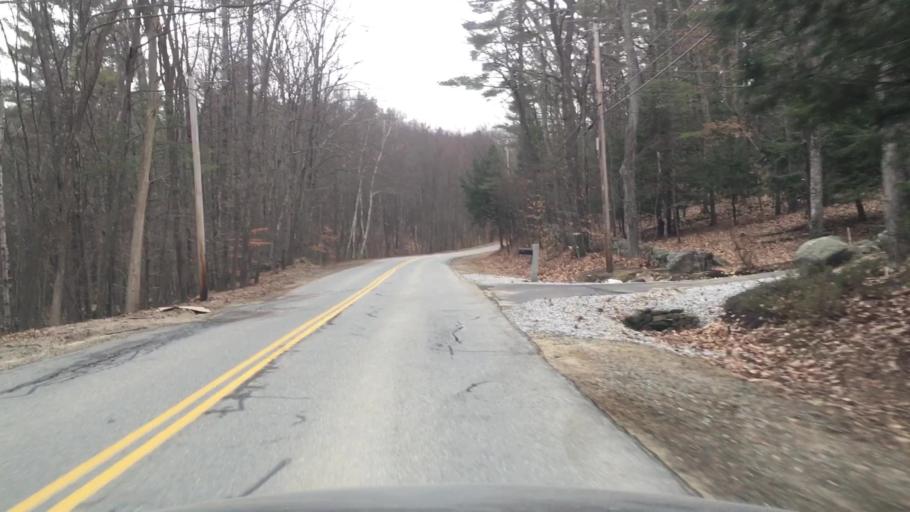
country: US
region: New Hampshire
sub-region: Hillsborough County
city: Mont Vernon
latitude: 42.9156
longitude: -71.5977
